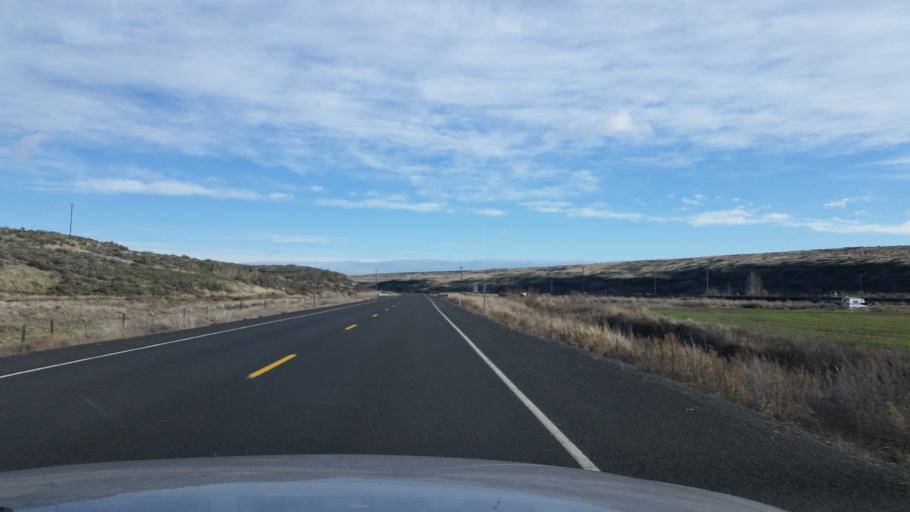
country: US
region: Washington
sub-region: Adams County
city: Ritzville
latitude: 47.3579
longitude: -118.5068
